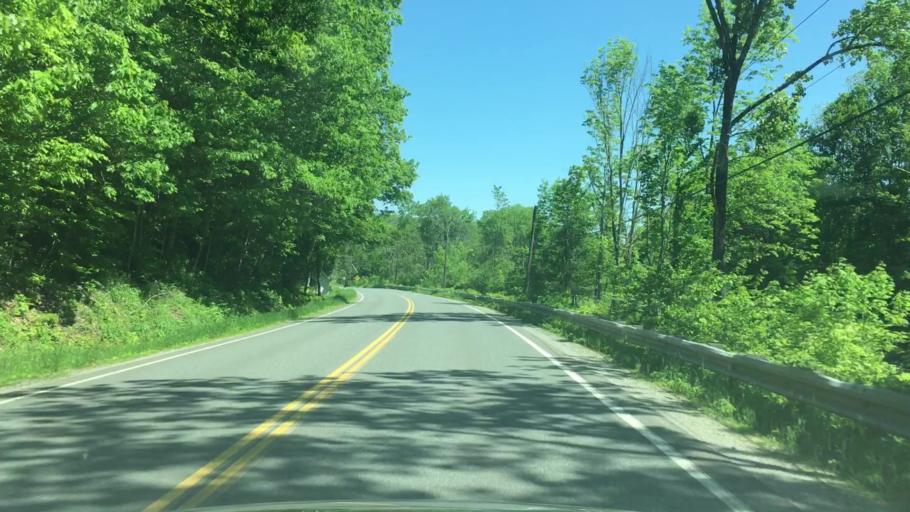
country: US
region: Massachusetts
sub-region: Franklin County
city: Colrain
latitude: 42.7307
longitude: -72.7168
